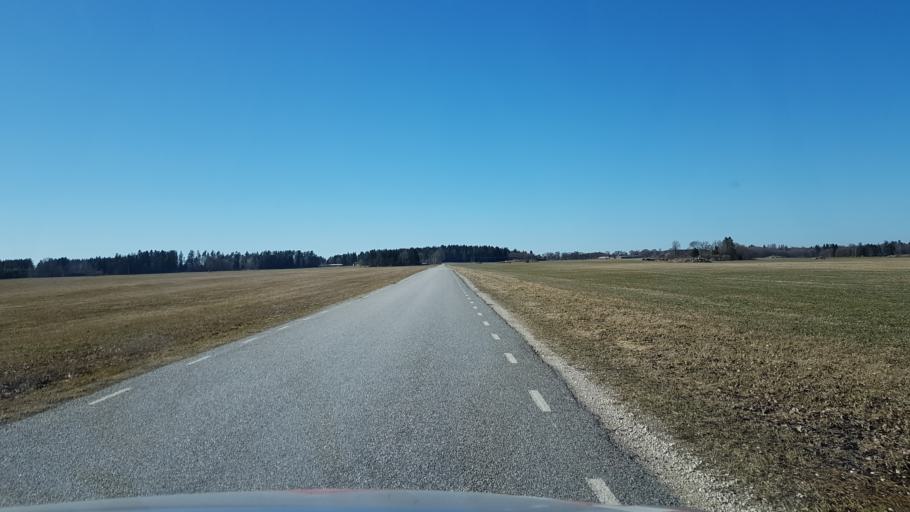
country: EE
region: Laeaene-Virumaa
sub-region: Viru-Nigula vald
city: Kunda
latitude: 59.4020
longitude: 26.5464
